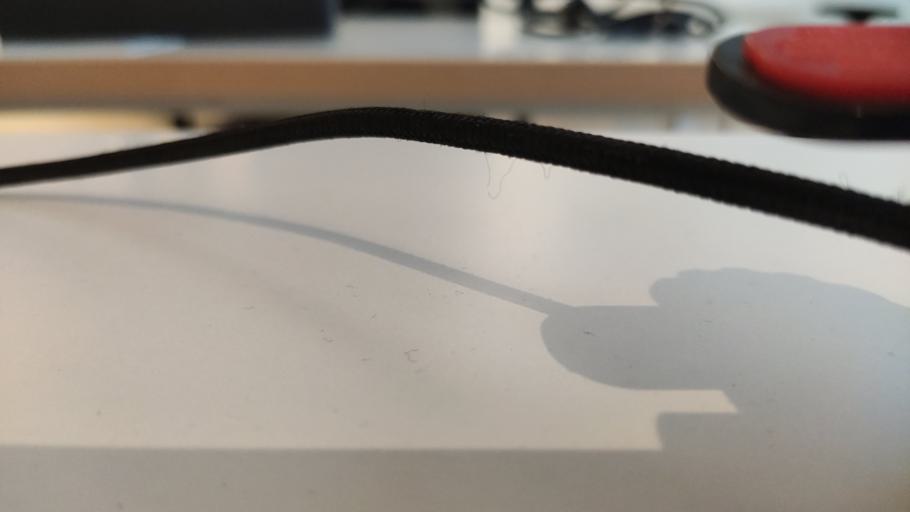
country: RU
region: Moskovskaya
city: Novopetrovskoye
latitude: 55.9047
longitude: 36.4410
